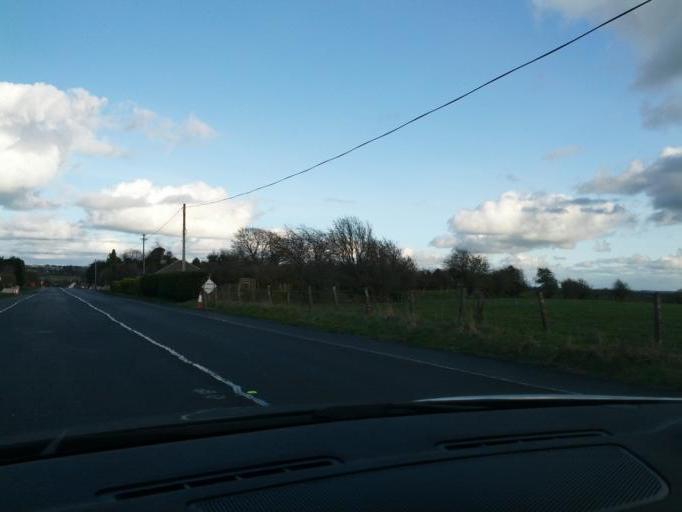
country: IE
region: Connaught
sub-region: Roscommon
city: Castlerea
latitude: 53.6902
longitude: -8.4205
